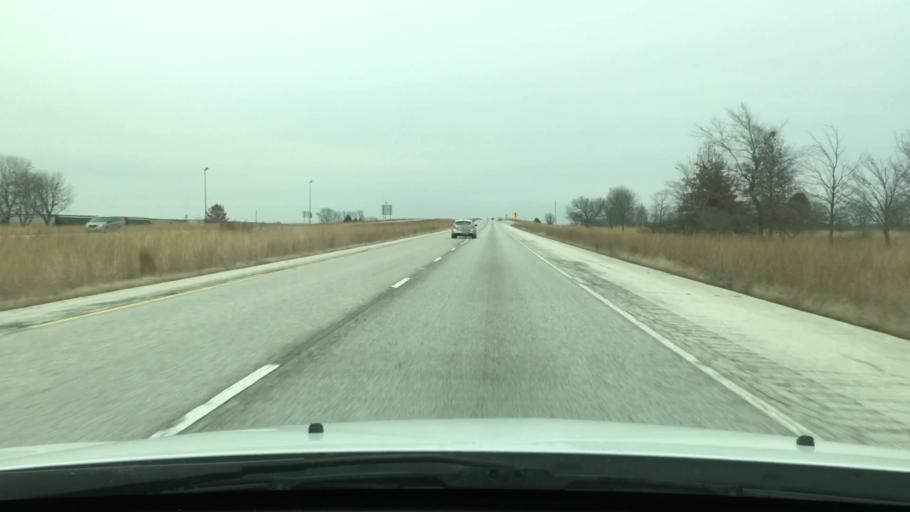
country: US
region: Illinois
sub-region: Morgan County
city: South Jacksonville
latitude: 39.6864
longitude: -90.2272
